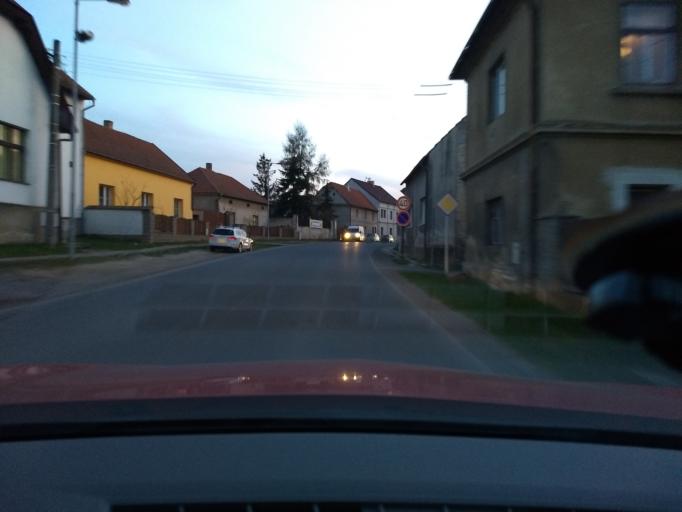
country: CZ
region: Central Bohemia
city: Rudna
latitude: 50.0617
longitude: 14.2311
